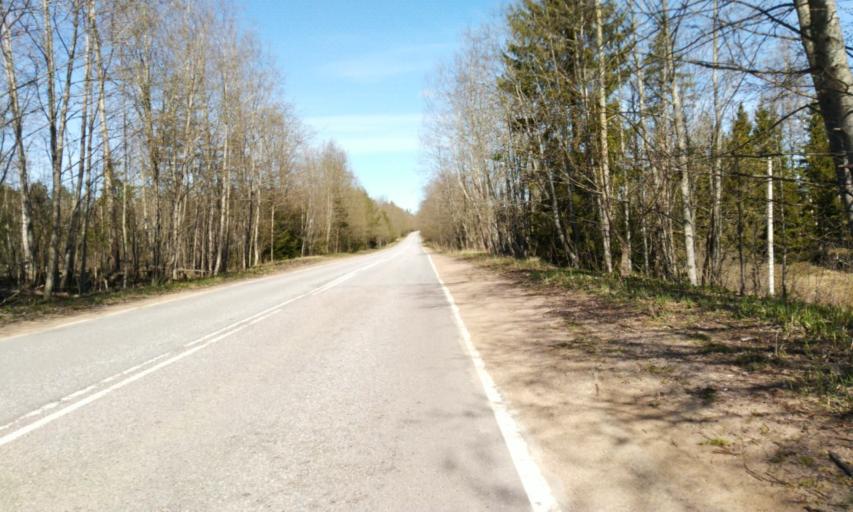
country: RU
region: Leningrad
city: Garbolovo
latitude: 60.4045
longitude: 30.4703
